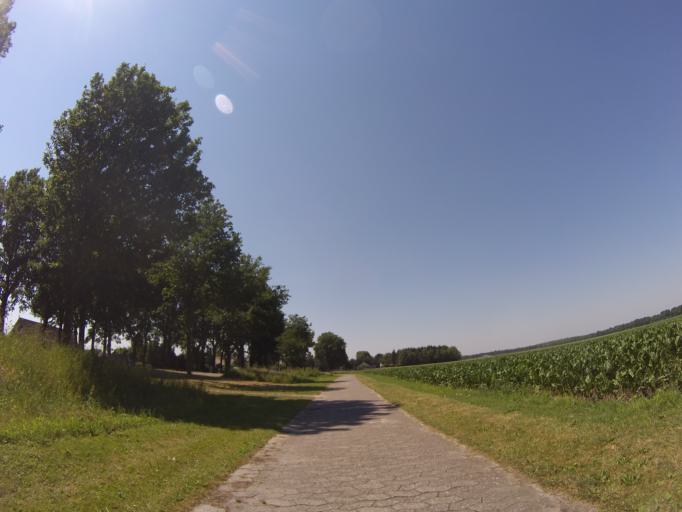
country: NL
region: Drenthe
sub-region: Gemeente Coevorden
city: Sleen
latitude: 52.8127
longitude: 6.8167
